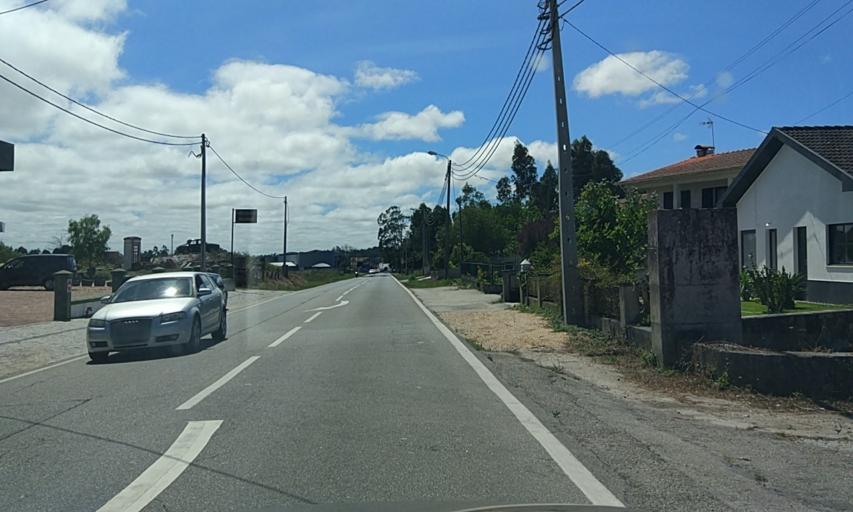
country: PT
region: Aveiro
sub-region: Vagos
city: Vagos
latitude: 40.5369
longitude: -8.6768
